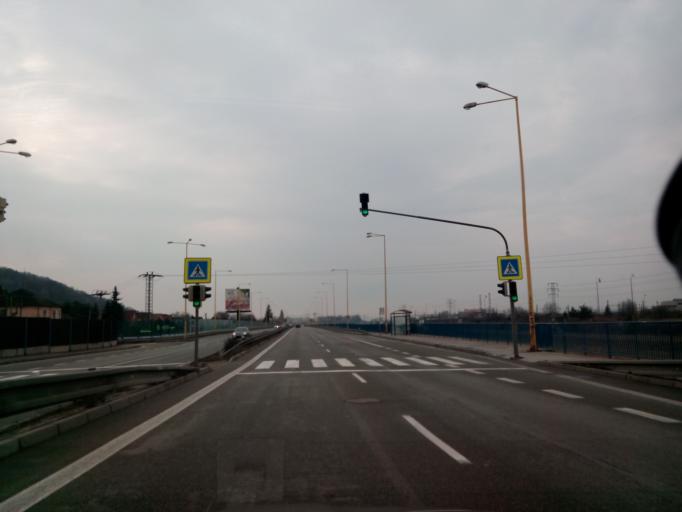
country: SK
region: Kosicky
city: Kosice
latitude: 48.7171
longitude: 21.2778
